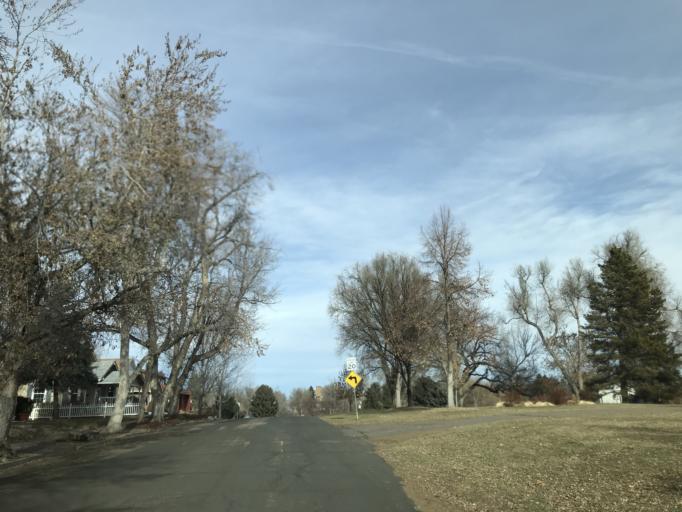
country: US
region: Colorado
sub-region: Arapahoe County
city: Littleton
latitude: 39.6082
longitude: -105.0116
